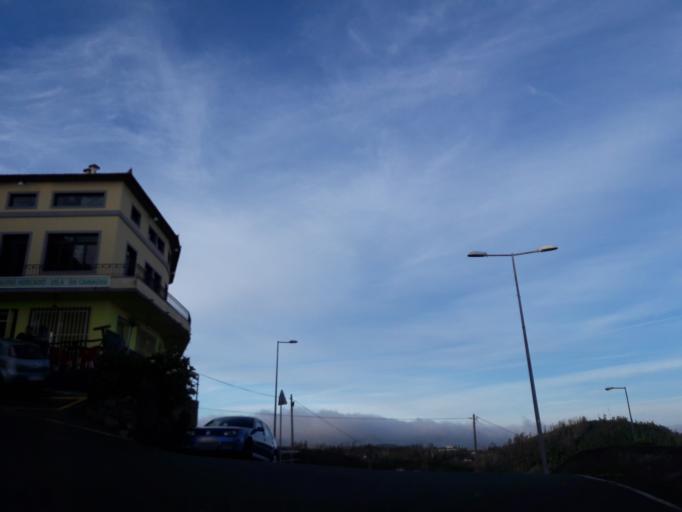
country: PT
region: Madeira
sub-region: Santa Cruz
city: Camacha
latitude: 32.6817
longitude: -16.8461
